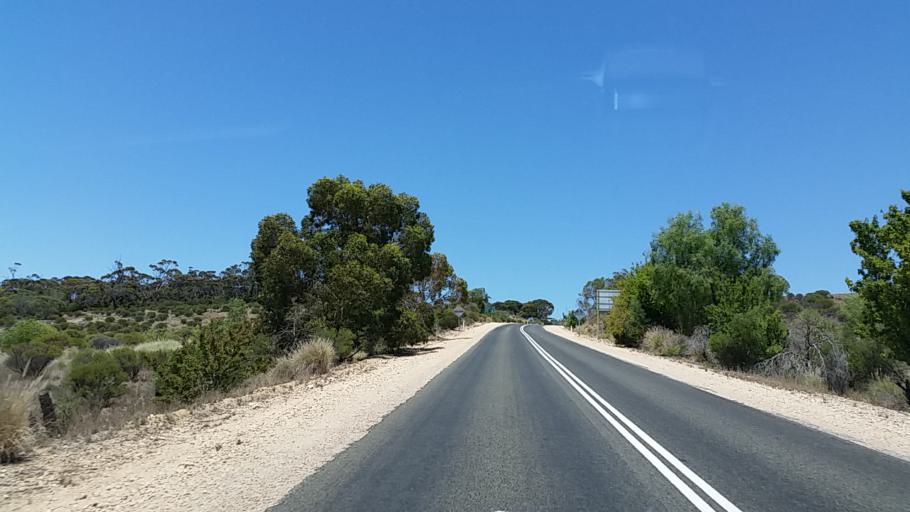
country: AU
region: South Australia
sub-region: Mid Murray
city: Mannum
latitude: -34.7540
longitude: 139.5555
